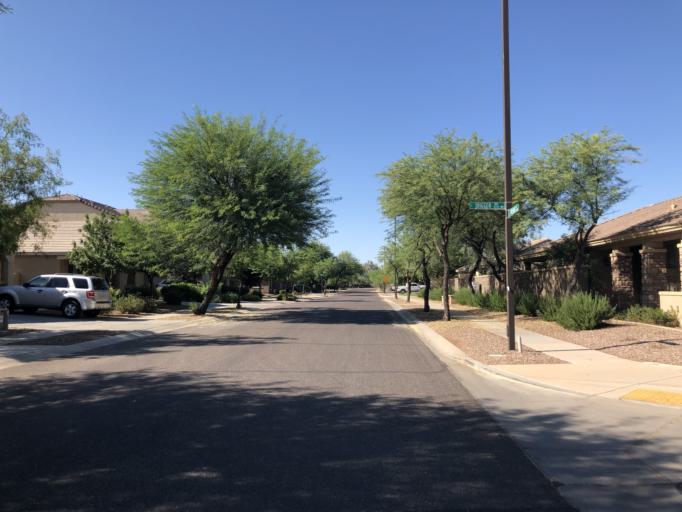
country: US
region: Arizona
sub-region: Maricopa County
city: Queen Creek
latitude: 33.2806
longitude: -111.6920
